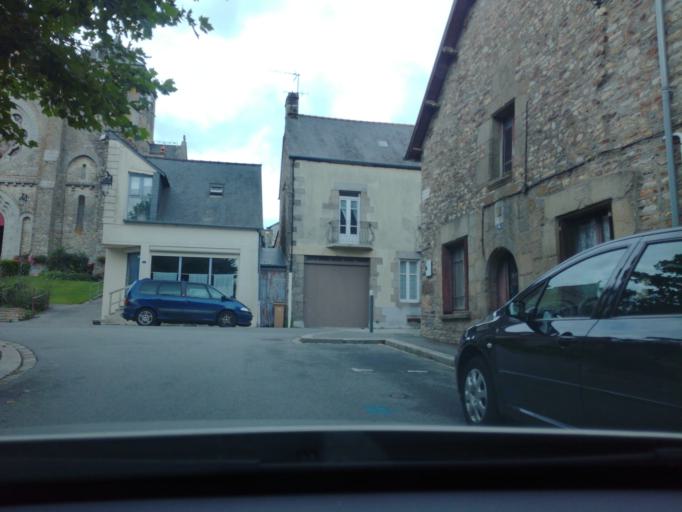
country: FR
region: Brittany
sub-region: Departement d'Ille-et-Vilaine
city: Saint-Aubin-du-Cormier
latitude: 48.2607
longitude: -1.3977
